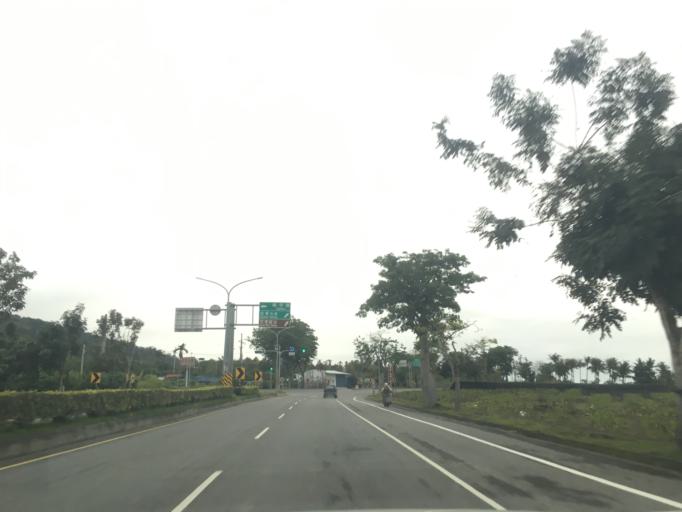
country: TW
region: Taiwan
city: Taitung City
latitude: 22.7120
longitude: 121.0448
